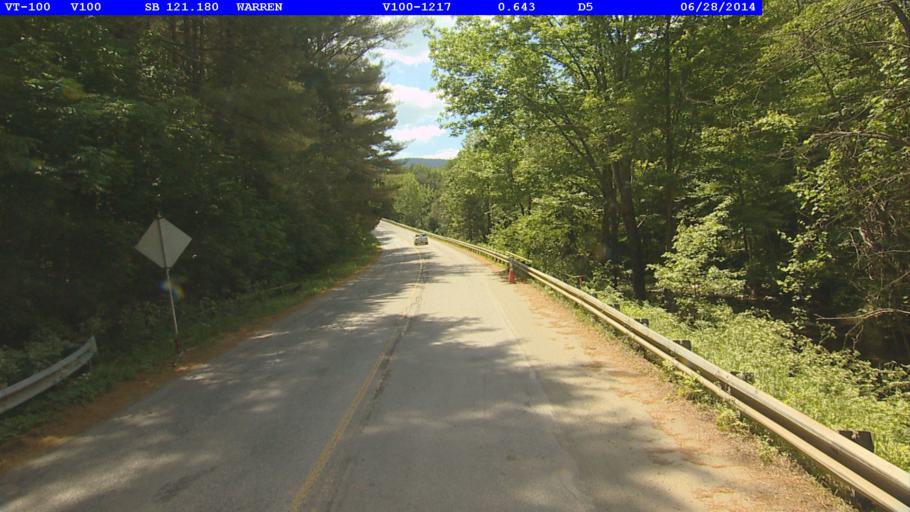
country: US
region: Vermont
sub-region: Washington County
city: Northfield
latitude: 44.0689
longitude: -72.8587
